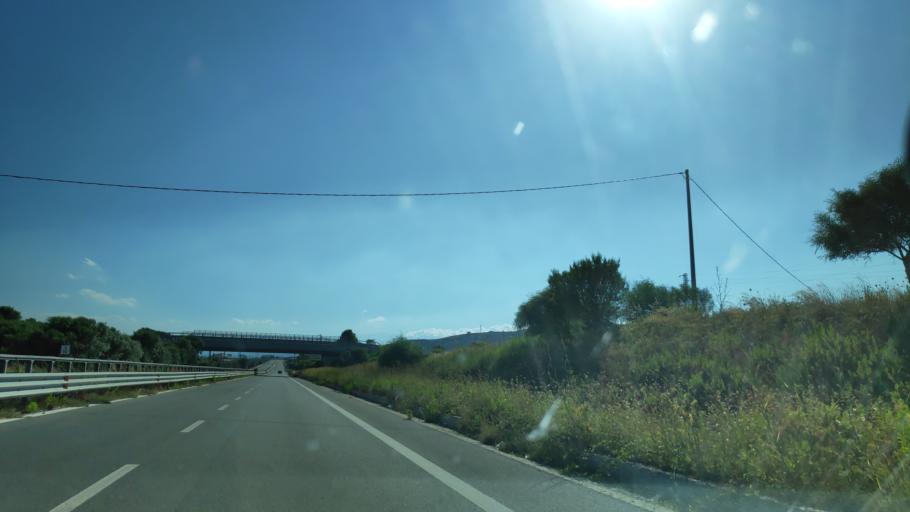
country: IT
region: Calabria
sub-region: Provincia di Reggio Calabria
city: Roccella Ionica
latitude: 38.3168
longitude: 16.3737
